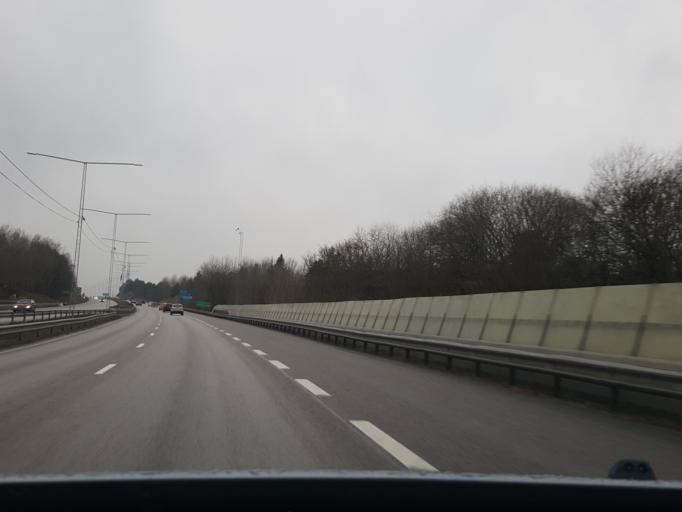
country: SE
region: Stockholm
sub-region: Lidingo
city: Brevik
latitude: 59.3162
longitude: 18.2030
